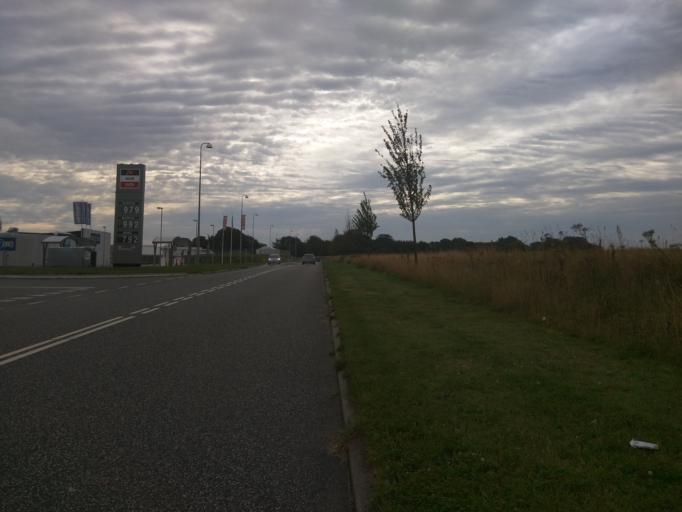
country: DK
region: Central Jutland
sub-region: Viborg Kommune
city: Viborg
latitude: 56.4458
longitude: 9.3633
